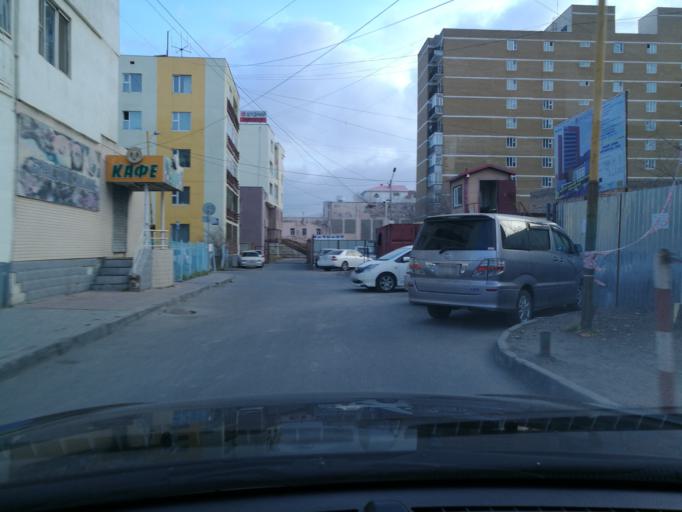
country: MN
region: Ulaanbaatar
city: Ulaanbaatar
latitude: 47.9218
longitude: 106.9258
